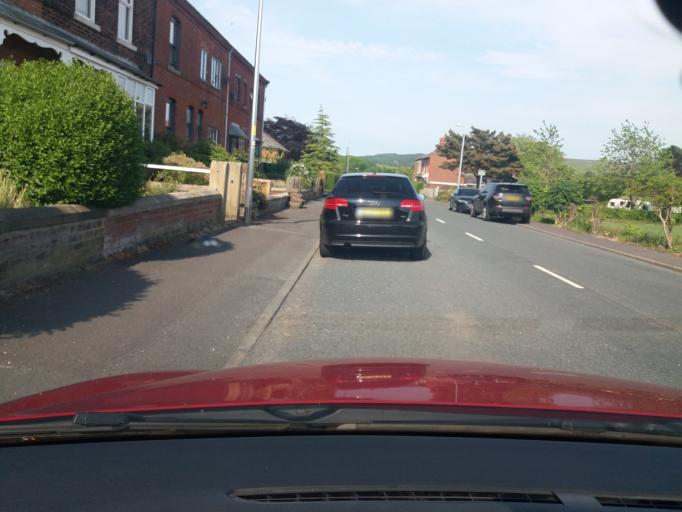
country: GB
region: England
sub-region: Lancashire
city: Chorley
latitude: 53.6660
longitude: -2.6094
